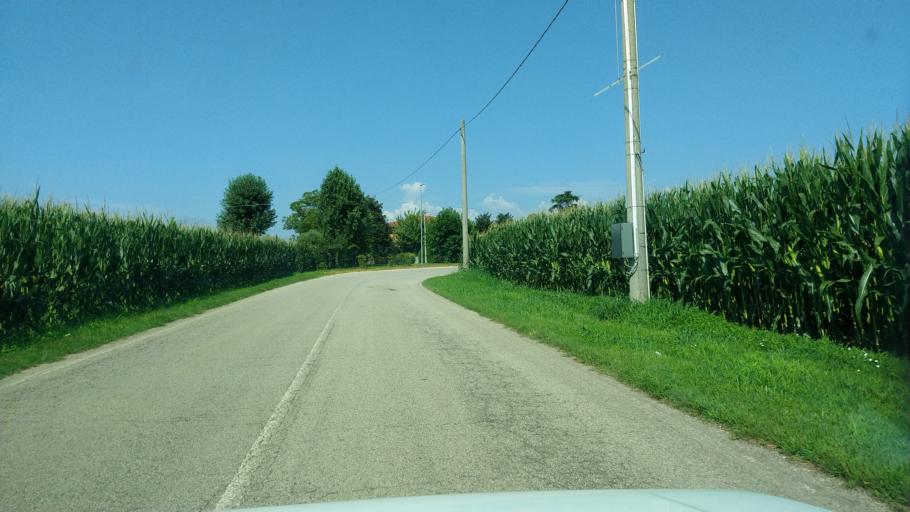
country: IT
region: Veneto
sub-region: Provincia di Vicenza
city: Sandrigo
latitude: 45.6801
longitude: 11.6074
